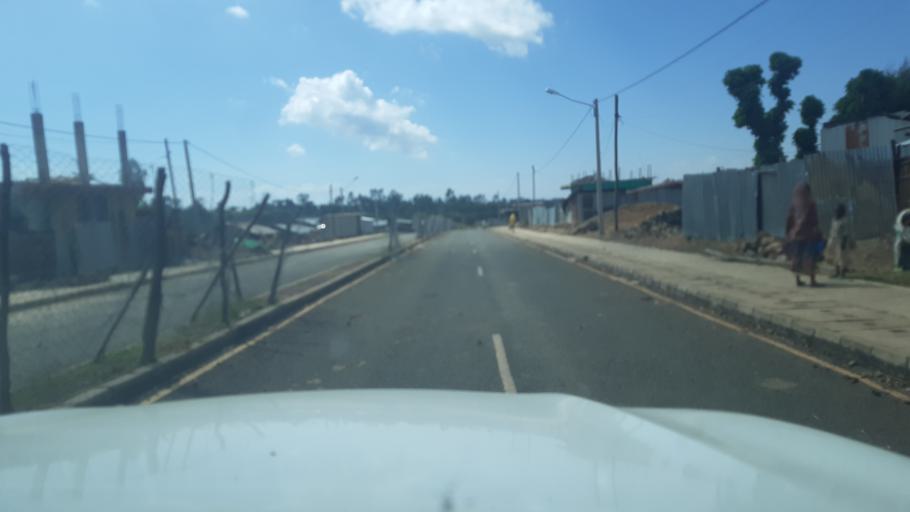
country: ET
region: Amhara
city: Dabat
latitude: 13.3924
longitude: 37.3998
